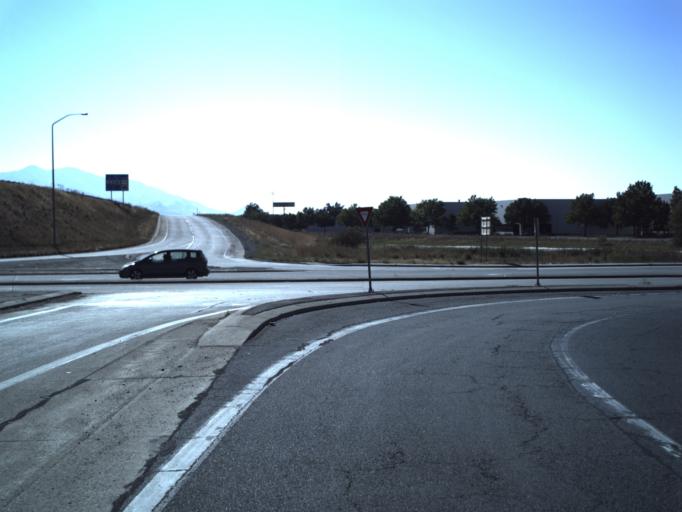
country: US
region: Utah
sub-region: Salt Lake County
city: West Valley City
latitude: 40.7273
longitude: -111.9674
